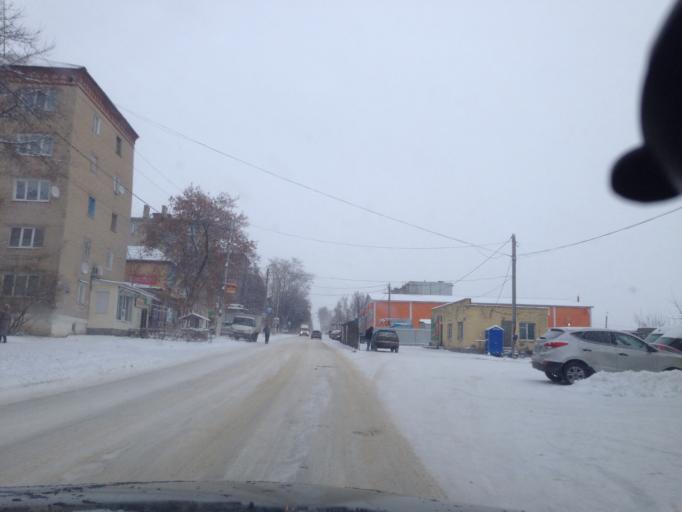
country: RU
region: Tula
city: Bolokhovo
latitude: 54.0821
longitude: 37.8275
